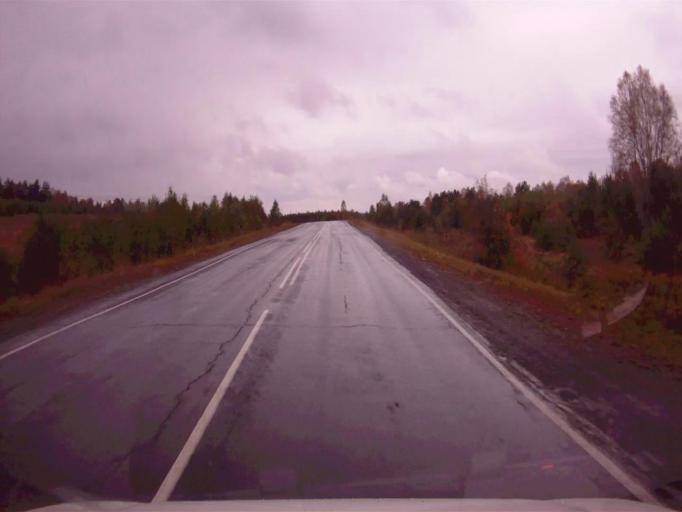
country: RU
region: Chelyabinsk
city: Verkhniy Ufaley
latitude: 56.0070
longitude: 60.3257
